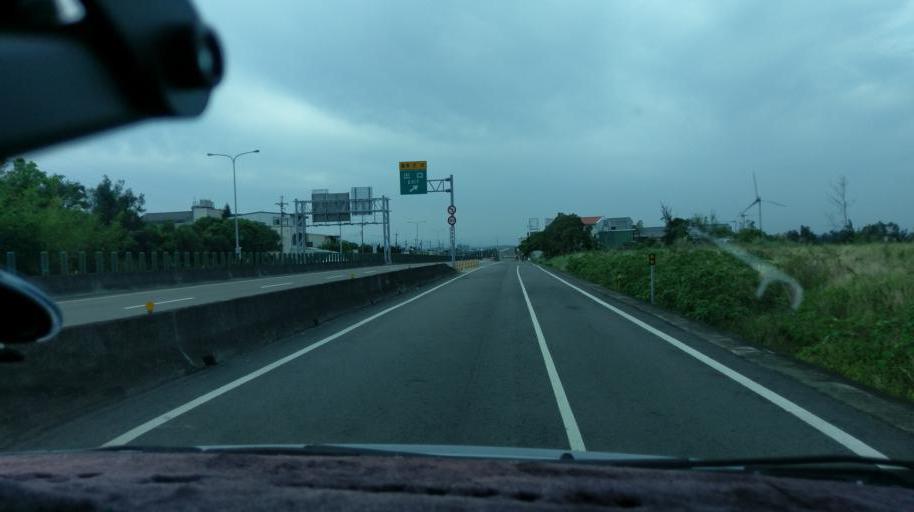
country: TW
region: Taiwan
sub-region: Hsinchu
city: Hsinchu
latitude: 24.7172
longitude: 120.8676
